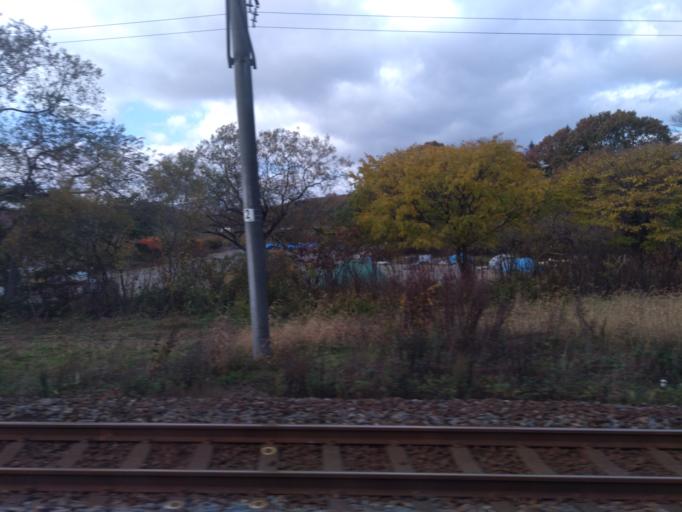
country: JP
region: Hokkaido
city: Shiraoi
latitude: 42.4553
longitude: 141.1866
